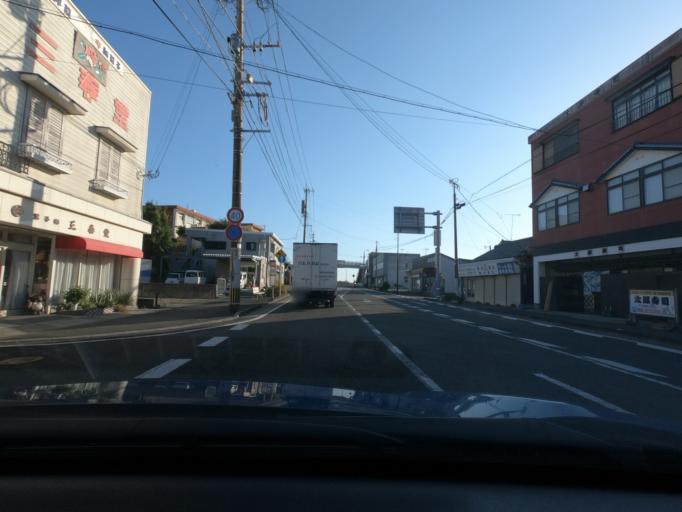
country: JP
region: Kagoshima
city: Akune
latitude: 32.0204
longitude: 130.1958
